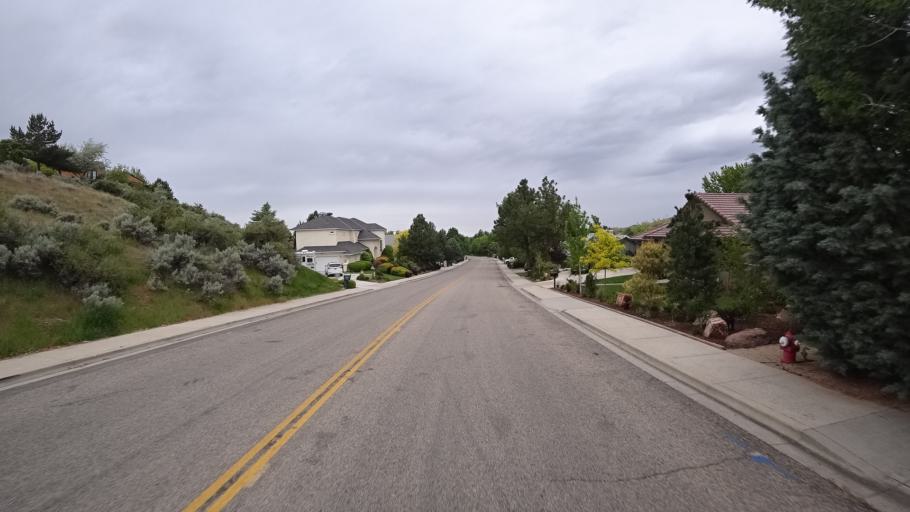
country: US
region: Idaho
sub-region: Ada County
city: Boise
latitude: 43.6139
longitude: -116.1589
